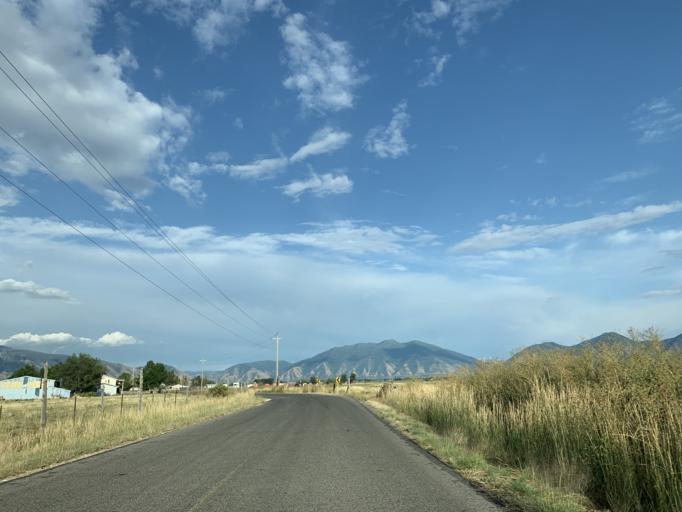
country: US
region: Utah
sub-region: Utah County
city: Benjamin
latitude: 40.1142
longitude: -111.7816
